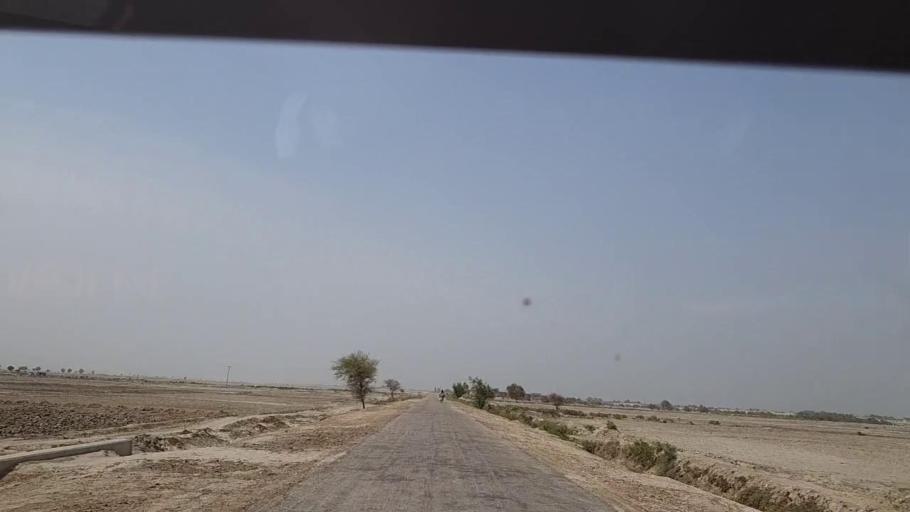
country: PK
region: Sindh
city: Khairpur Nathan Shah
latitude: 27.0581
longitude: 67.6479
